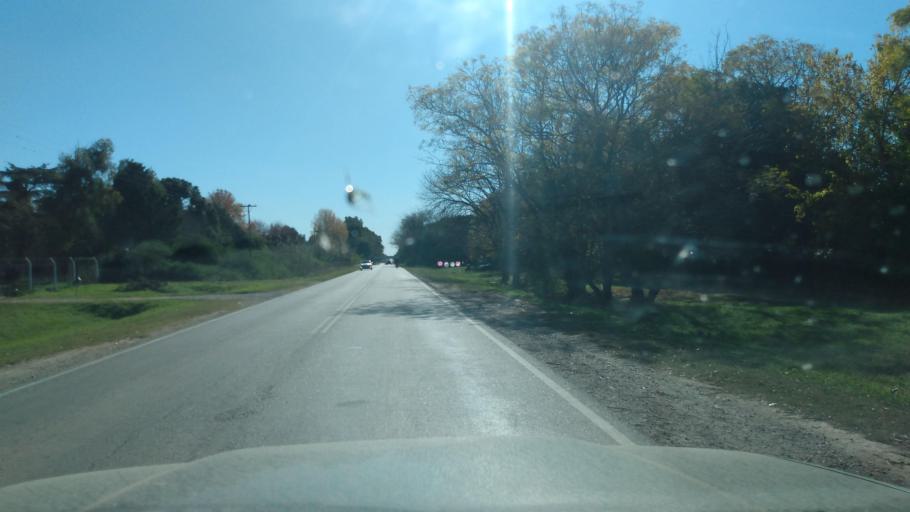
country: AR
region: Buenos Aires
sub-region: Partido de Lujan
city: Lujan
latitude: -34.5368
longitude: -59.1630
